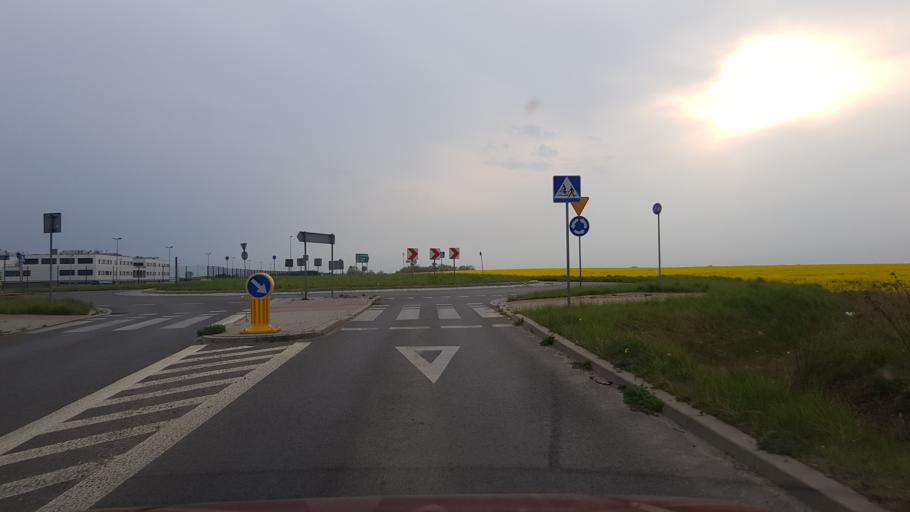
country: PL
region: West Pomeranian Voivodeship
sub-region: Powiat pyrzycki
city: Bielice
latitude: 53.2654
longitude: 14.6431
